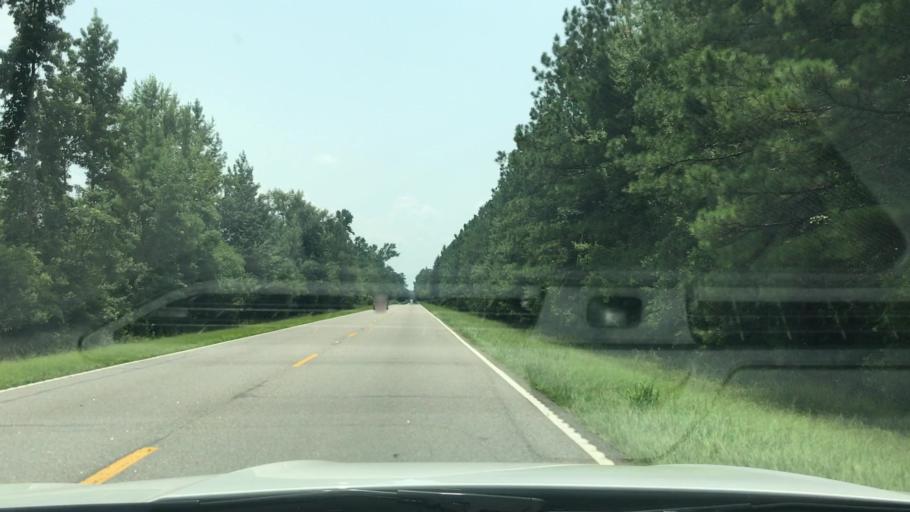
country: US
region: South Carolina
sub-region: Georgetown County
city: Georgetown
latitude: 33.5374
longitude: -79.2323
